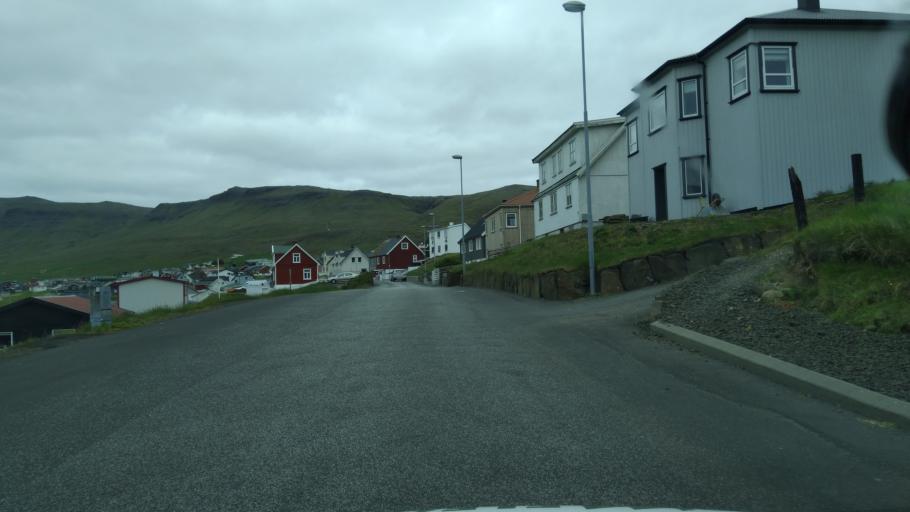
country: FO
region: Suduroy
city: Tvoroyri
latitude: 61.5608
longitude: -6.8261
